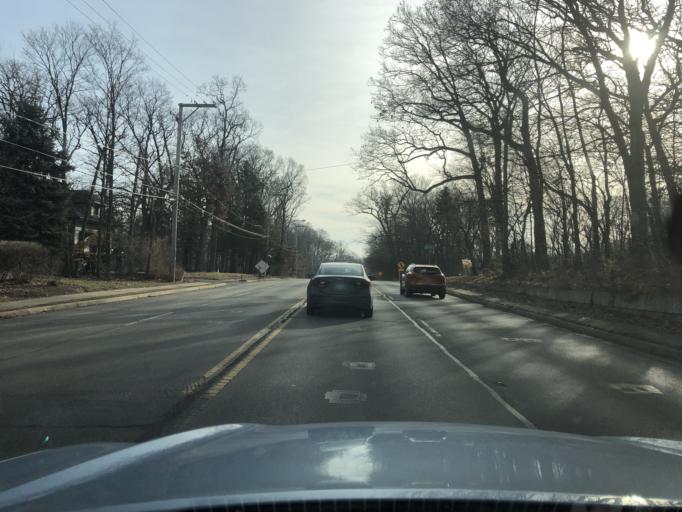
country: US
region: Illinois
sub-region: DuPage County
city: Bloomingdale
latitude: 41.9708
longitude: -88.0803
